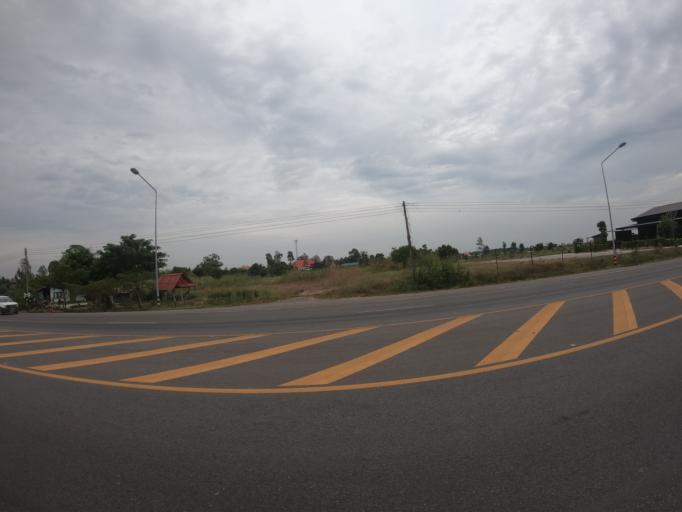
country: TH
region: Roi Et
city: Chiang Khwan
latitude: 16.1452
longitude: 103.8585
